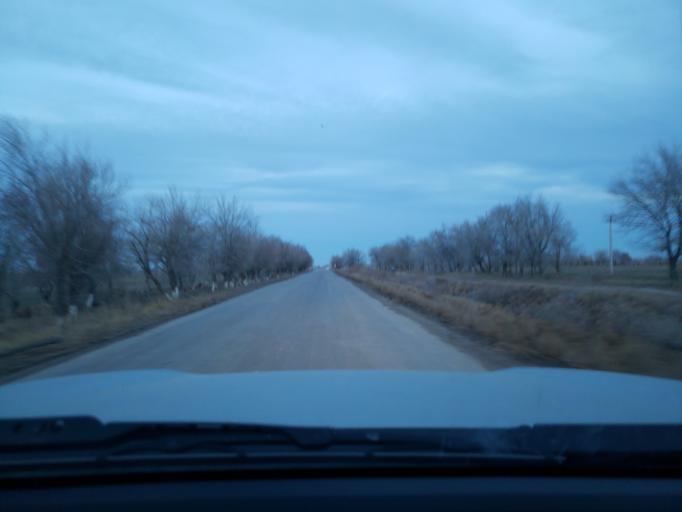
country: TM
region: Dasoguz
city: Tagta
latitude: 41.6227
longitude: 60.0586
